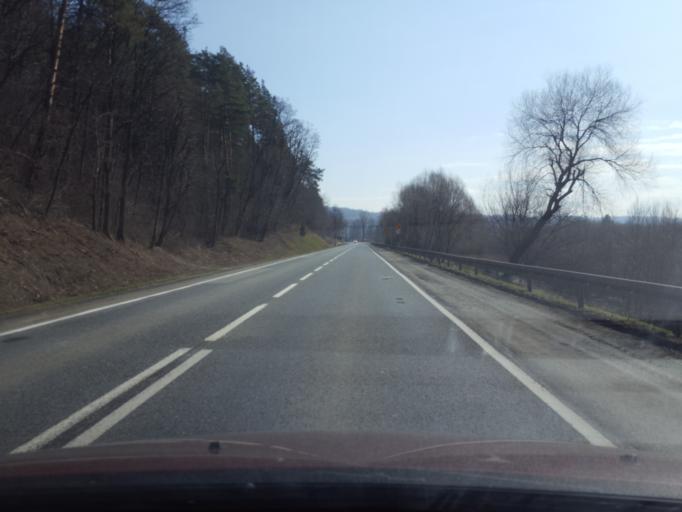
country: PL
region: Lesser Poland Voivodeship
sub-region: Powiat nowosadecki
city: Chelmiec
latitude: 49.6759
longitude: 20.6602
